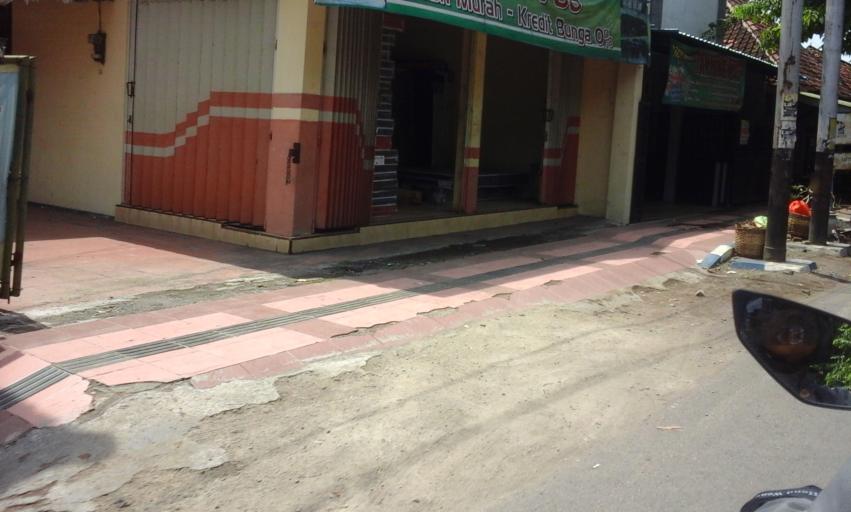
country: ID
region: East Java
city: Kebunjeruk
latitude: -8.1919
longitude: 114.3773
